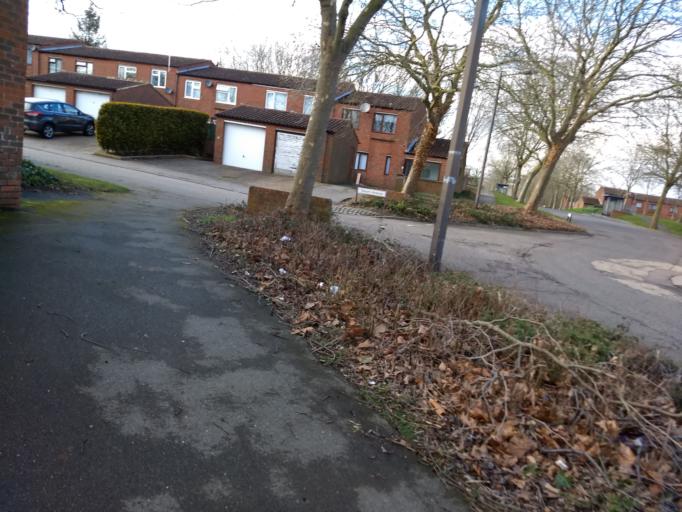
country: GB
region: England
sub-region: Milton Keynes
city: Milton Keynes
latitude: 52.0412
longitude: -0.7369
